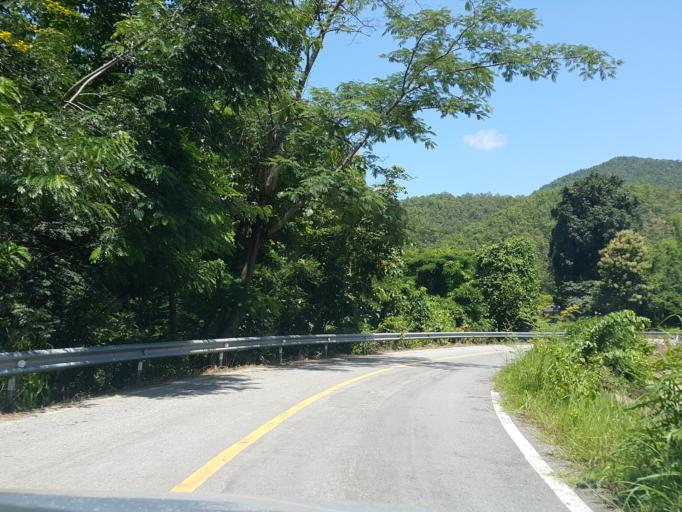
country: TH
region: Chiang Mai
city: San Kamphaeng
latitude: 18.6910
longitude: 99.1770
